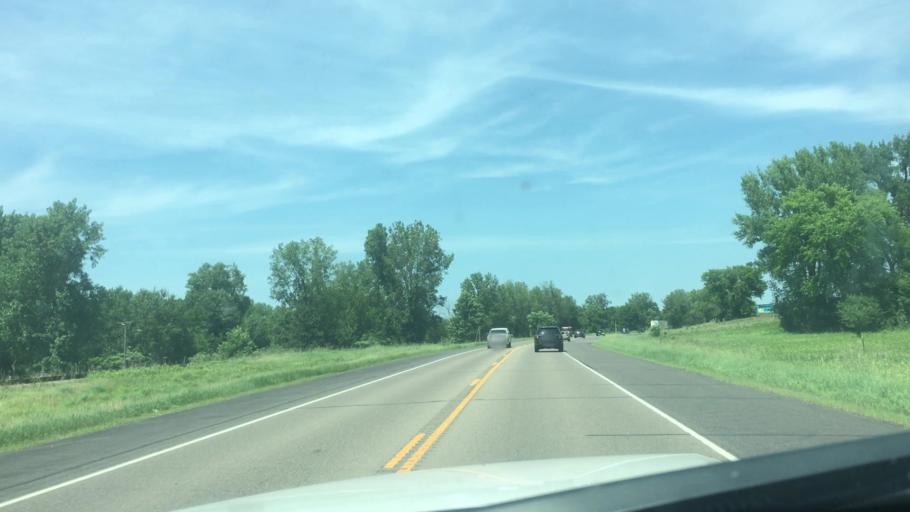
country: US
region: Minnesota
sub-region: Ramsey County
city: White Bear Lake
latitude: 45.1169
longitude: -93.0025
